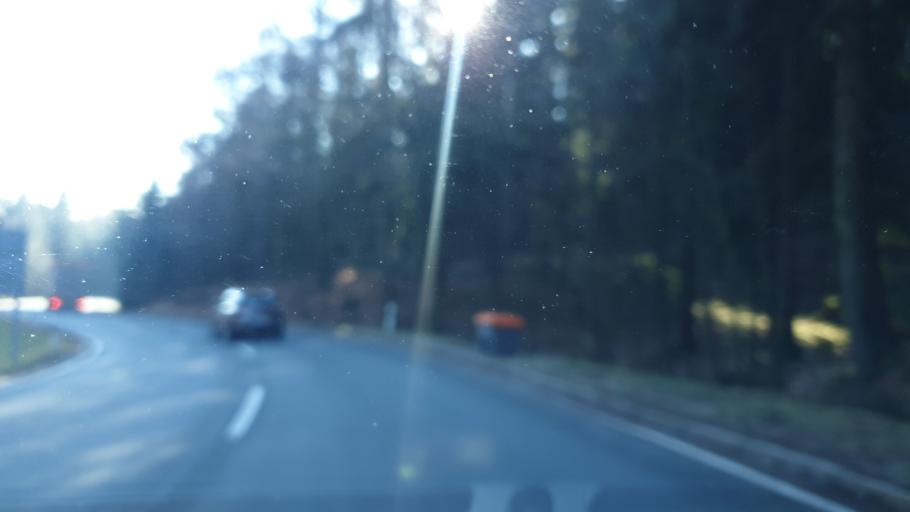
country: DE
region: Saxony
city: Bad Brambach
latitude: 50.1945
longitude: 12.3142
